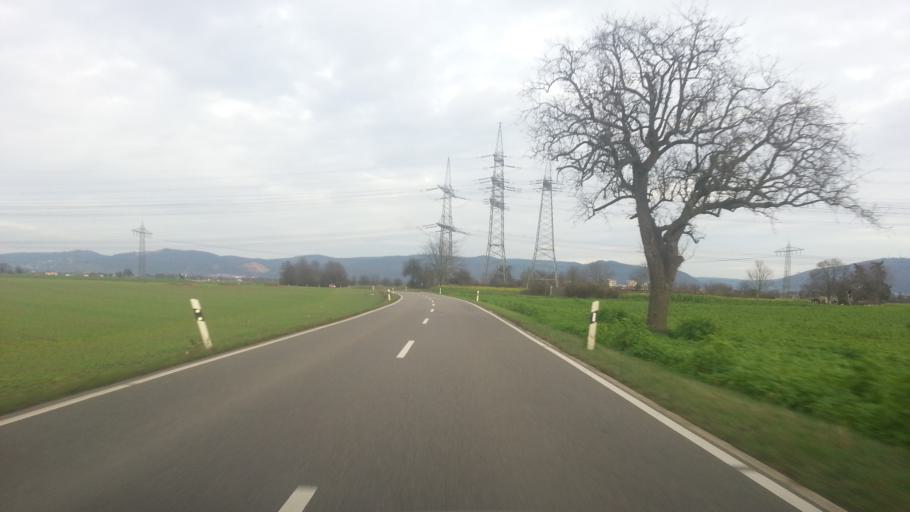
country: DE
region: Baden-Wuerttemberg
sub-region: Karlsruhe Region
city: Plankstadt
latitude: 49.4008
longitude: 8.6043
